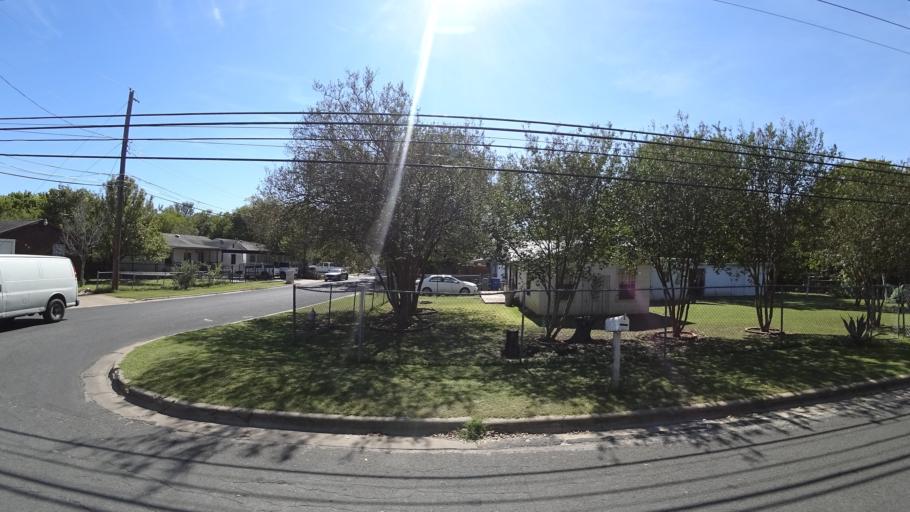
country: US
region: Texas
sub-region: Travis County
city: Austin
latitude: 30.2694
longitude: -97.6806
